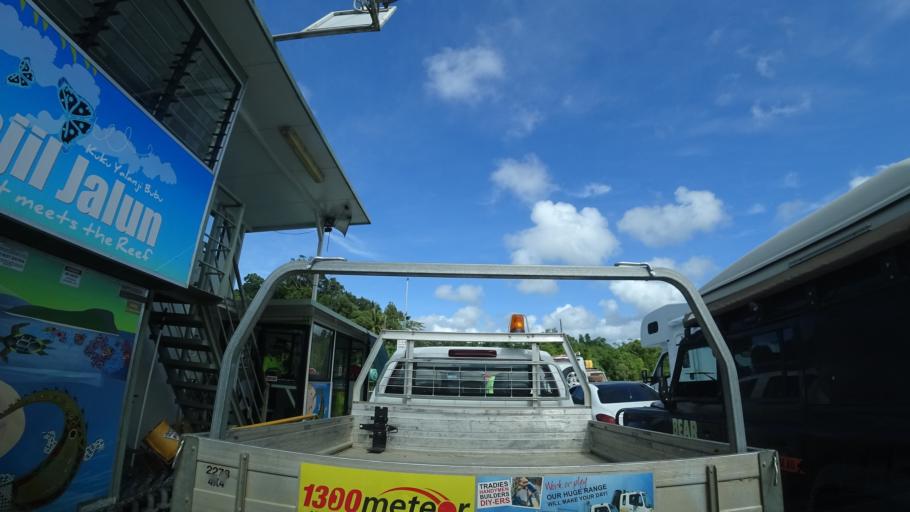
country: AU
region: Queensland
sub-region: Cairns
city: Port Douglas
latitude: -16.2588
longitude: 145.3988
